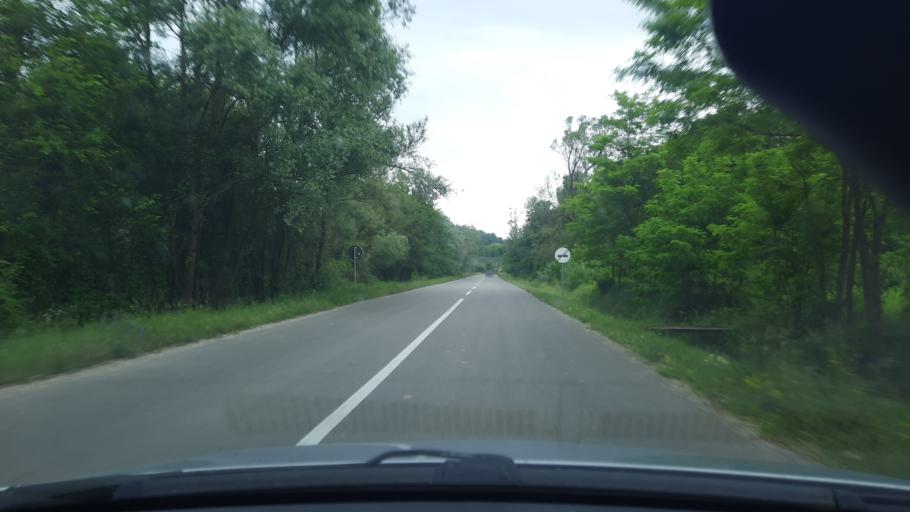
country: RS
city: Jarebice
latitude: 44.4976
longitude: 19.4855
